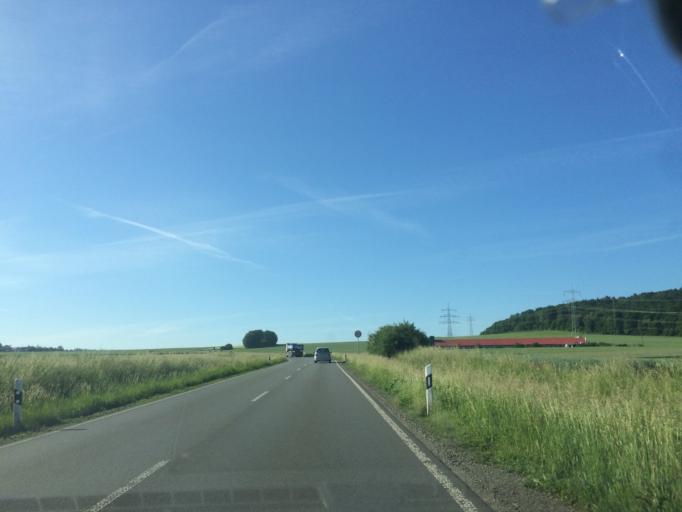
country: DE
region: Hesse
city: Trendelburg
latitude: 51.5340
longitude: 9.4108
